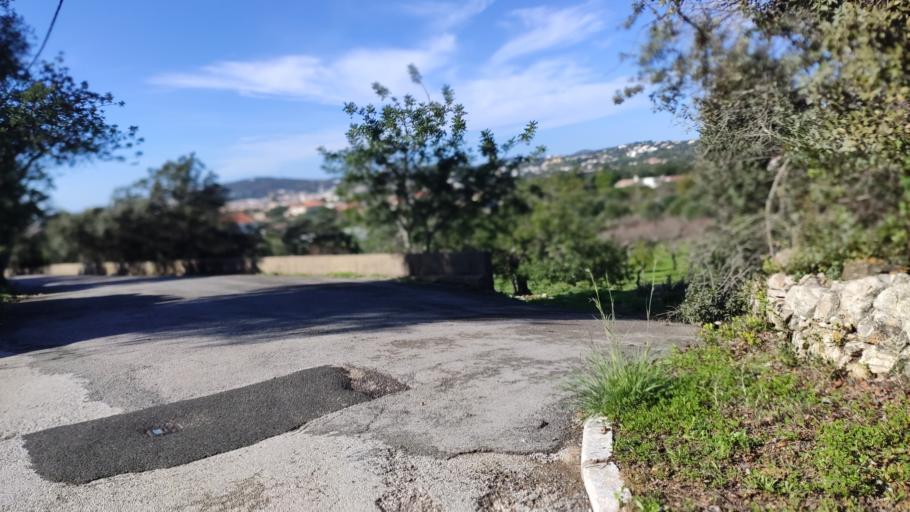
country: PT
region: Faro
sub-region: Sao Bras de Alportel
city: Sao Bras de Alportel
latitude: 37.1513
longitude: -7.8688
